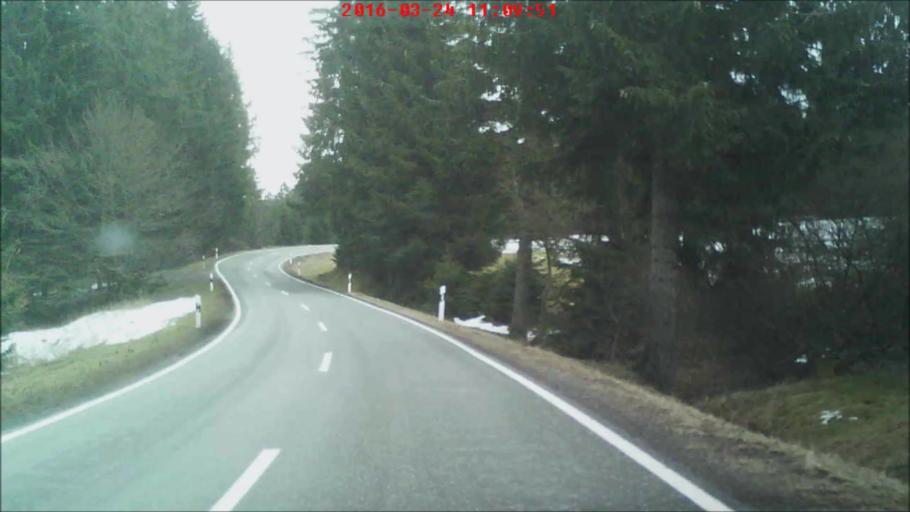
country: DE
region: Thuringia
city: Masserberg
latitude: 50.5308
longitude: 10.9509
